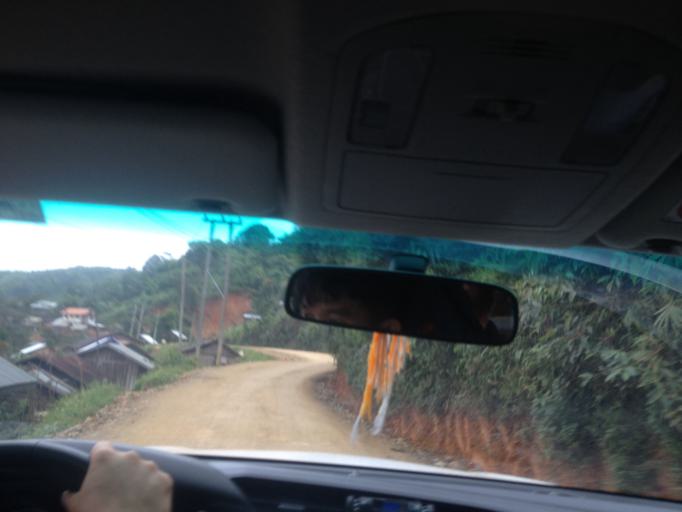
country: TH
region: Nan
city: Chaloem Phra Kiat
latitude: 19.9820
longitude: 101.1435
